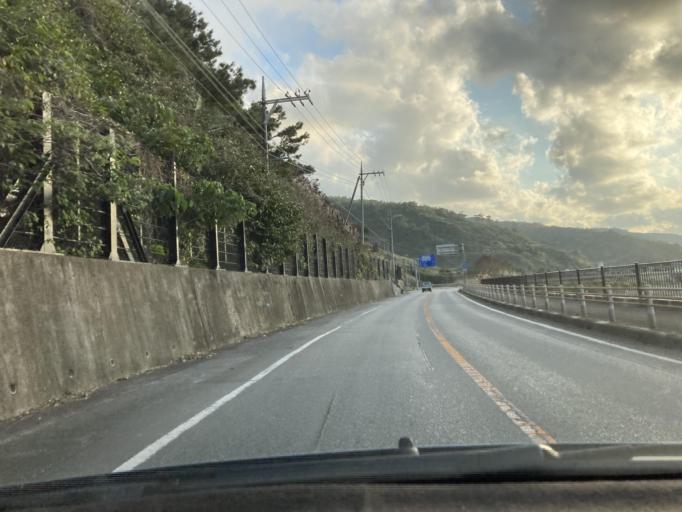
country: JP
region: Okinawa
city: Nago
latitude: 26.7898
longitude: 128.2242
